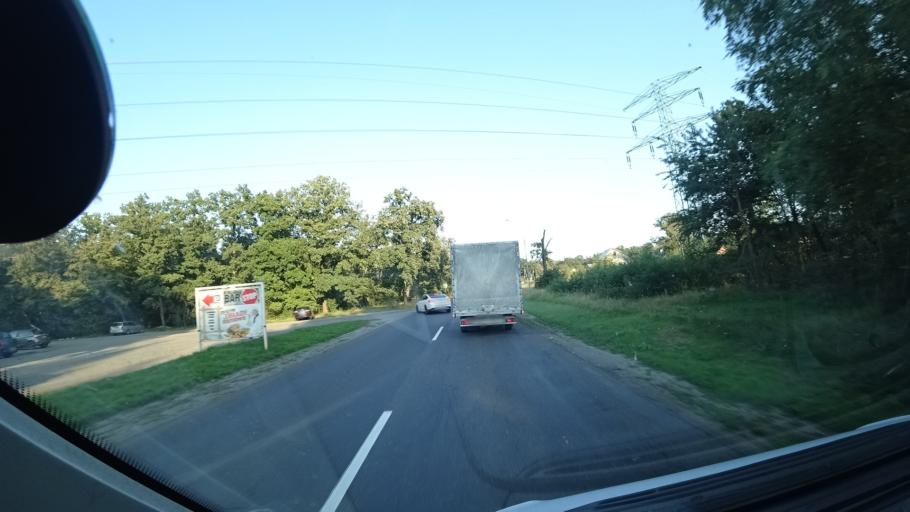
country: PL
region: Opole Voivodeship
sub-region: Powiat kedzierzynsko-kozielski
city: Dziergowice
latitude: 50.2848
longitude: 18.2895
